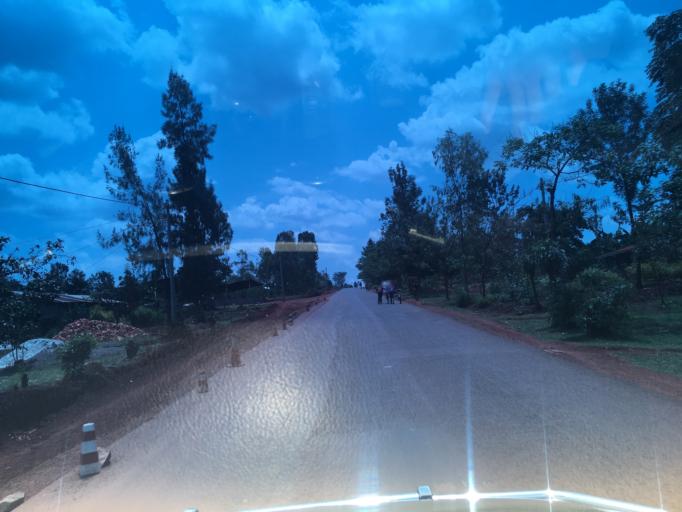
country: RW
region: Eastern Province
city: Kibungo
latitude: -2.2768
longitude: 30.6008
